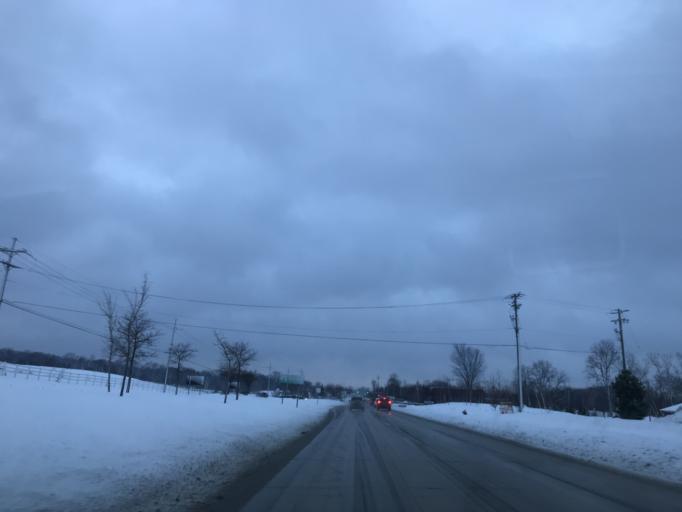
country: US
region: Michigan
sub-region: Oakland County
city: Novi
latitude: 42.4958
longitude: -83.4619
